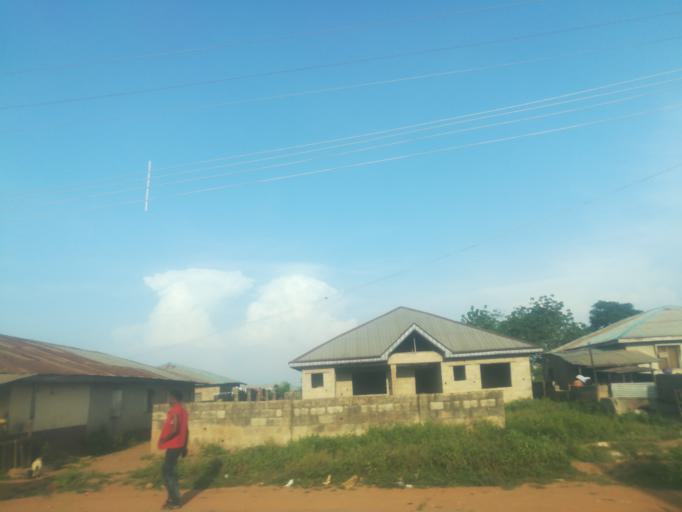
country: NG
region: Oyo
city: Moniya
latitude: 7.5630
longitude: 3.8861
